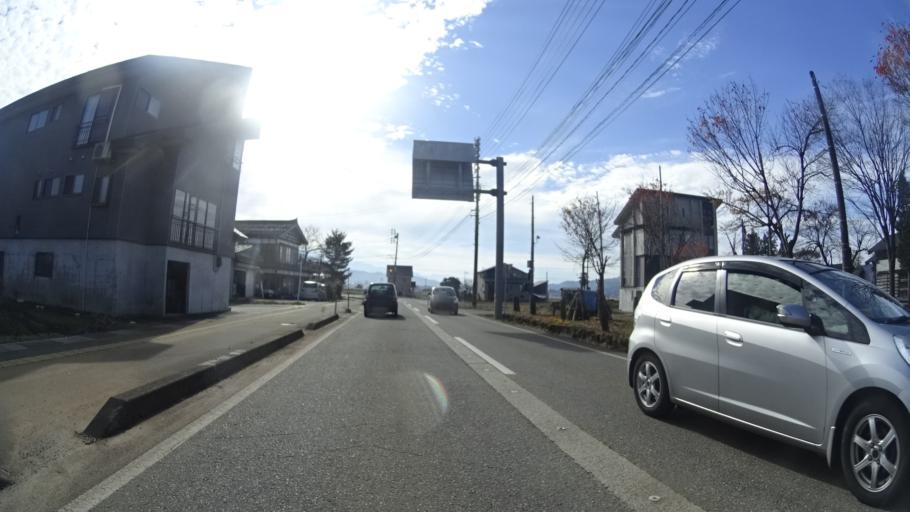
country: JP
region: Niigata
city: Ojiya
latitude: 37.2553
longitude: 138.9815
